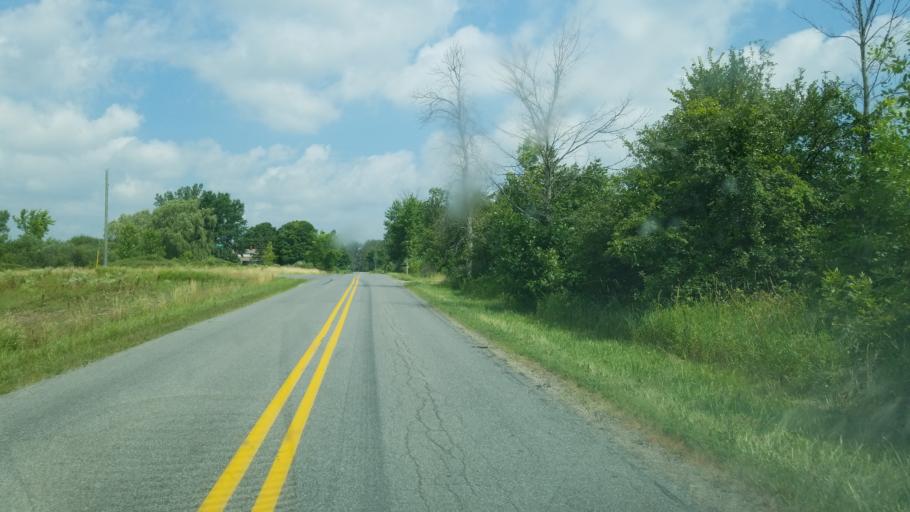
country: US
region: Michigan
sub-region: Kent County
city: Cedar Springs
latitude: 43.2596
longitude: -85.5113
